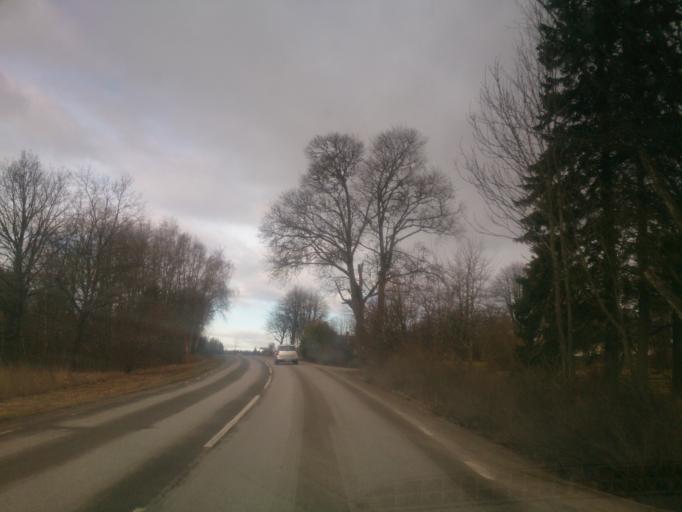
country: SE
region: OEstergoetland
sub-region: Motala Kommun
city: Stenstorp
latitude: 58.5156
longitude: 15.0916
